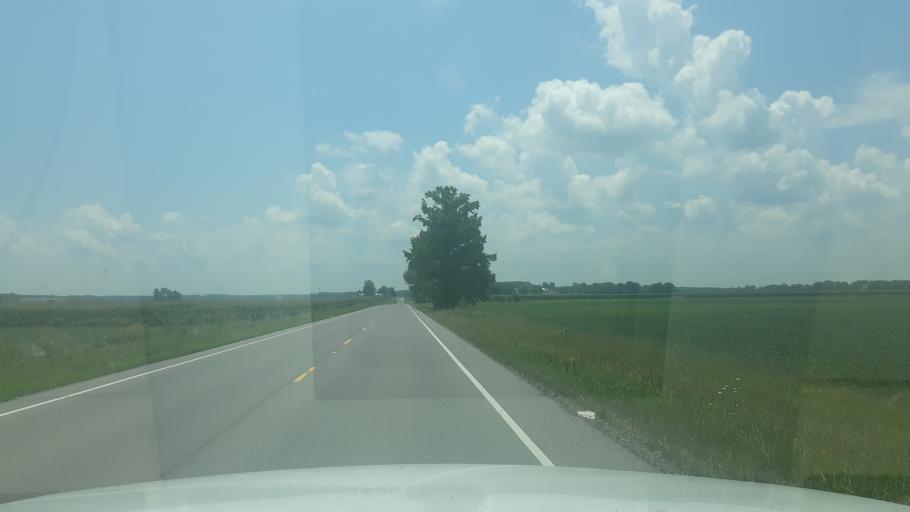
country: US
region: Illinois
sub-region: Saline County
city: Harrisburg
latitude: 37.8097
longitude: -88.5397
